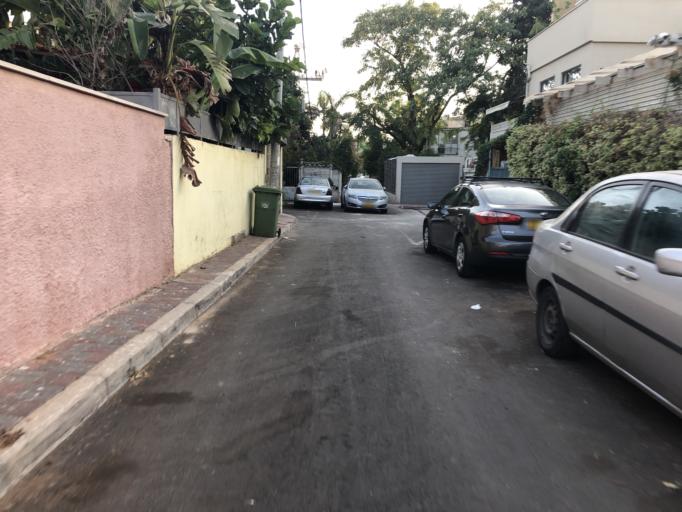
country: IL
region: Tel Aviv
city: Giv`atayim
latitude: 32.0695
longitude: 34.8186
